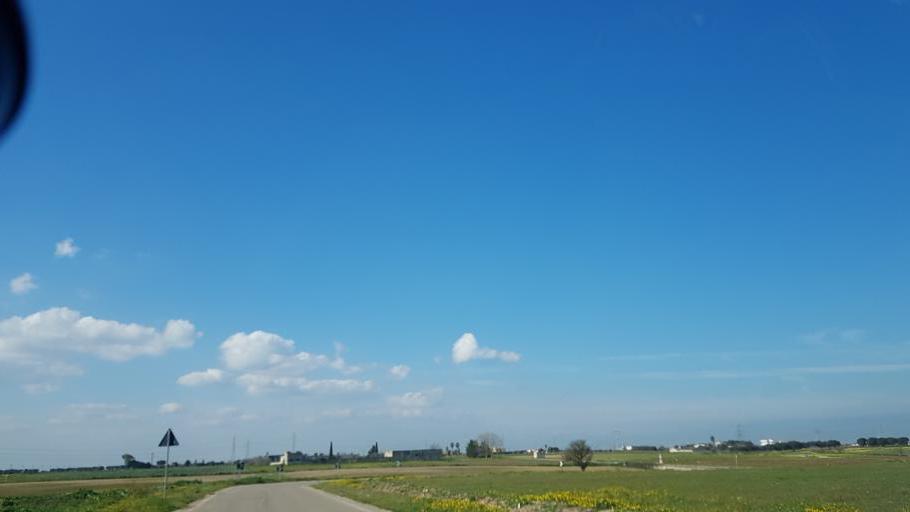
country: IT
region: Apulia
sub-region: Provincia di Brindisi
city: La Rosa
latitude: 40.5904
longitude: 17.9211
